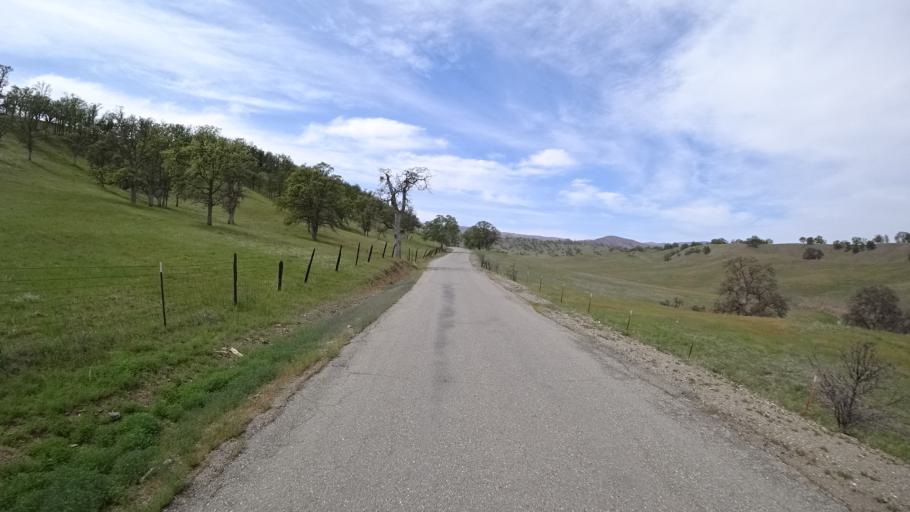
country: US
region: California
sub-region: Glenn County
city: Willows
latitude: 39.6100
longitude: -122.5613
